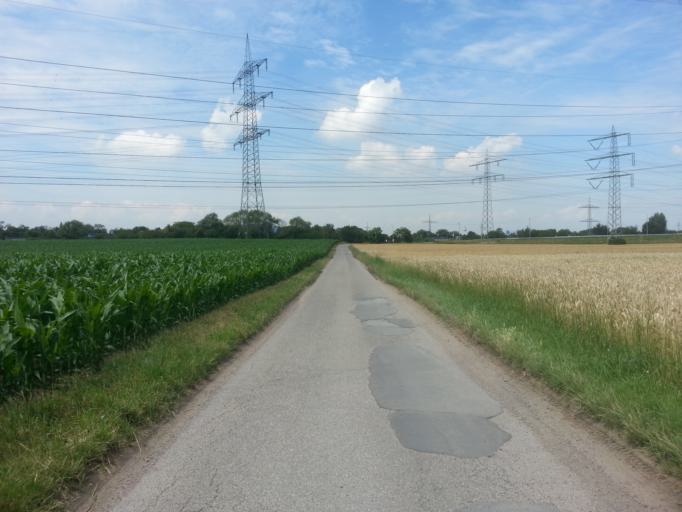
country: DE
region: Baden-Wuerttemberg
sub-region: Karlsruhe Region
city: Ilvesheim
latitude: 49.4549
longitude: 8.5460
